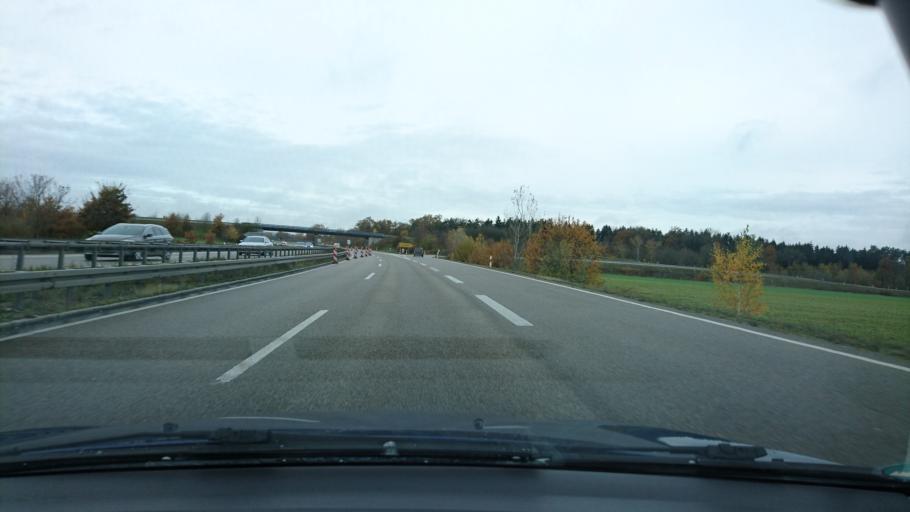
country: DE
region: Bavaria
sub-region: Swabia
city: Langweid
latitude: 48.5019
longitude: 10.8583
